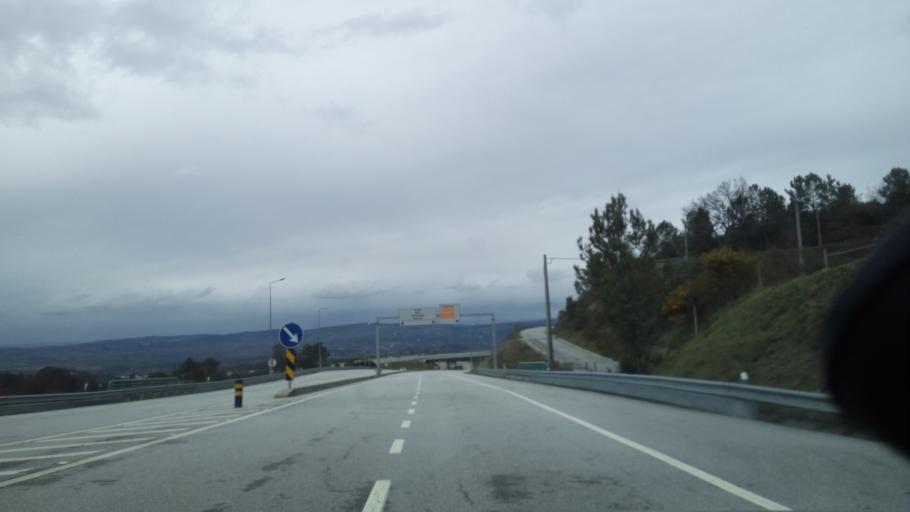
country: PT
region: Guarda
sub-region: Manteigas
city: Manteigas
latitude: 40.4835
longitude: -7.5978
